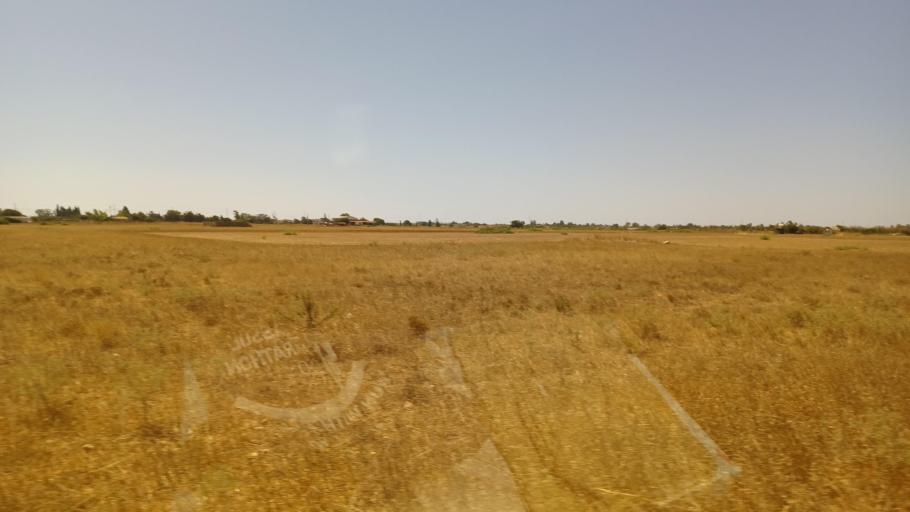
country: CY
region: Ammochostos
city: Avgorou
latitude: 35.0507
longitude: 33.8474
